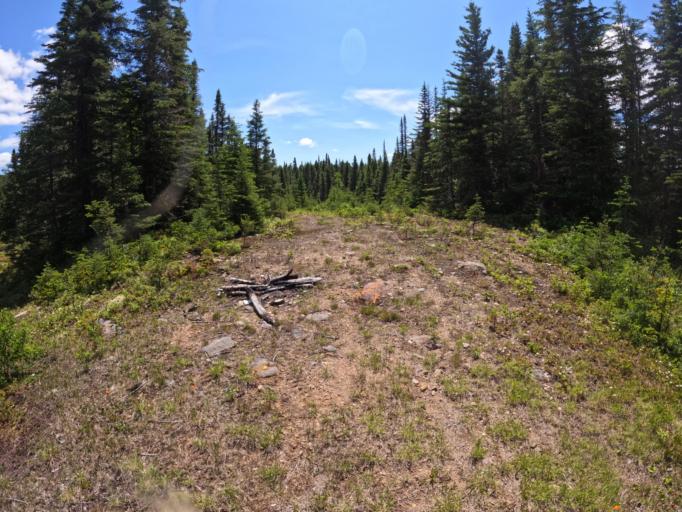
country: CA
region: Quebec
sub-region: Capitale-Nationale
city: Baie-Saint-Paul
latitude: 47.7393
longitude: -70.6615
